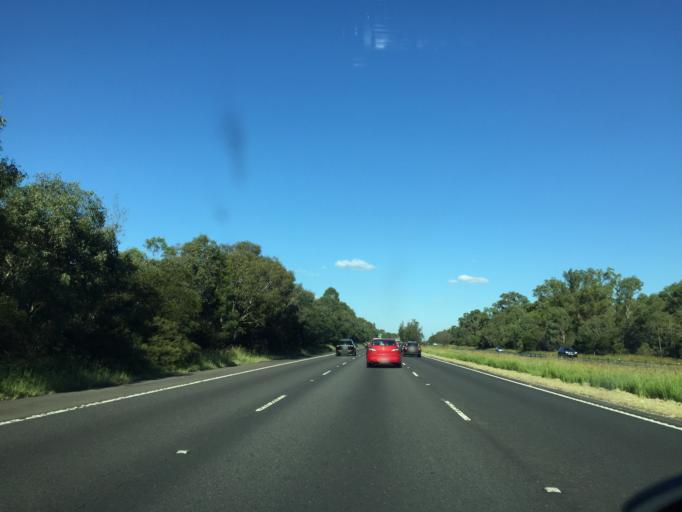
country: AU
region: New South Wales
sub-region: Penrith Municipality
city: Kingswood Park
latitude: -33.7832
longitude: 150.7397
